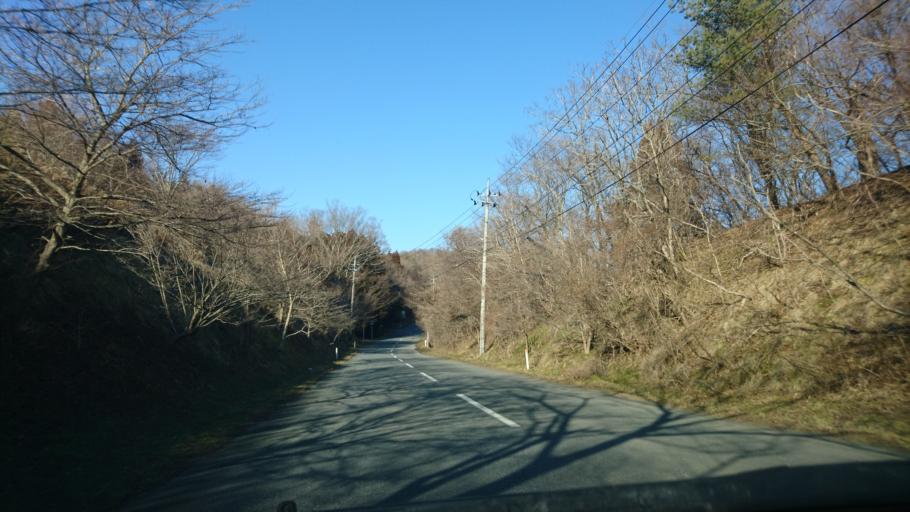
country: JP
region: Iwate
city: Ichinoseki
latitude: 38.8222
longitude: 141.2796
